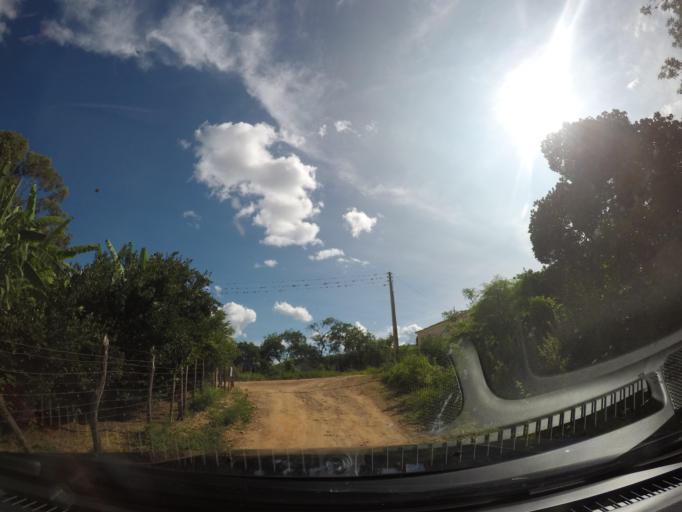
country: BR
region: Bahia
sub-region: Barra Da Estiva
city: Barra da Estiva
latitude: -13.1959
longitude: -41.5889
